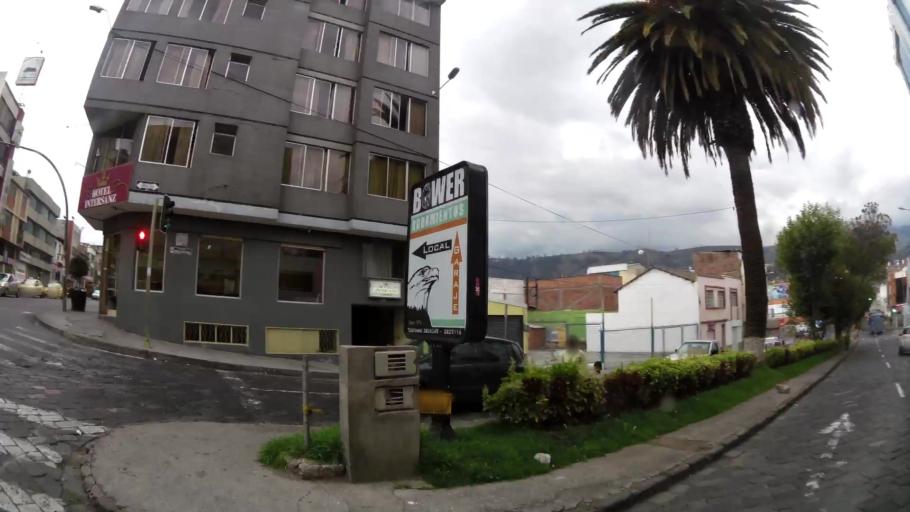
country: EC
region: Tungurahua
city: Ambato
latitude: -1.2372
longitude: -78.6211
